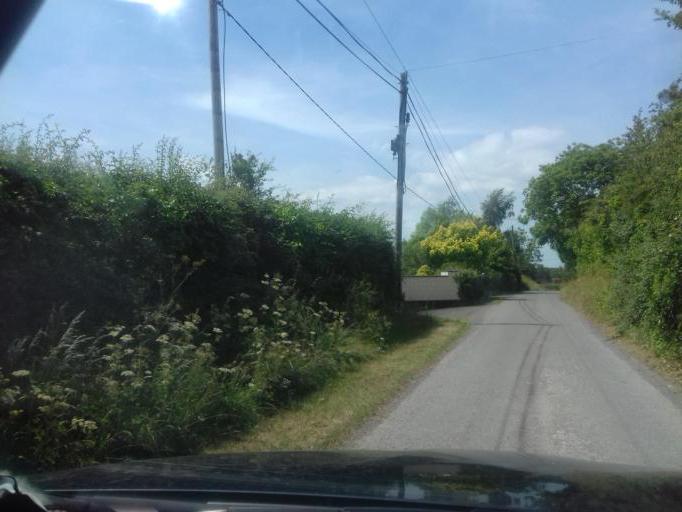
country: IE
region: Leinster
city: Lusk
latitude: 53.5351
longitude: -6.1593
